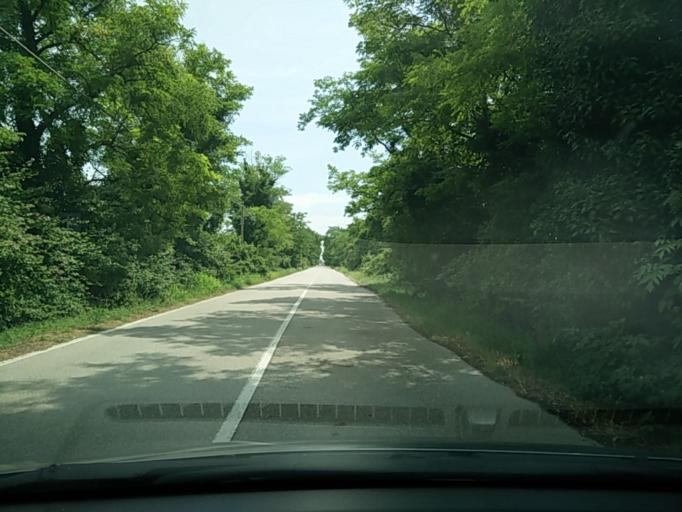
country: IT
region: Veneto
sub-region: Provincia di Venezia
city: San Liberale
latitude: 45.5238
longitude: 12.3612
